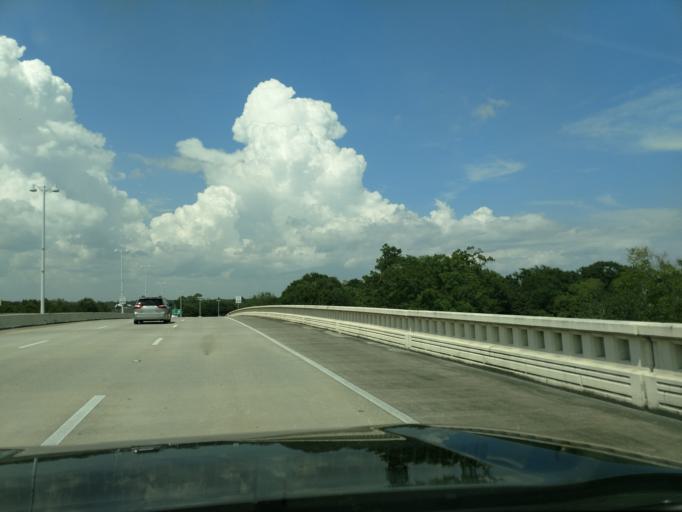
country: US
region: Mississippi
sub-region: Jackson County
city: Ocean Springs
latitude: 30.4136
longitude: -88.8377
